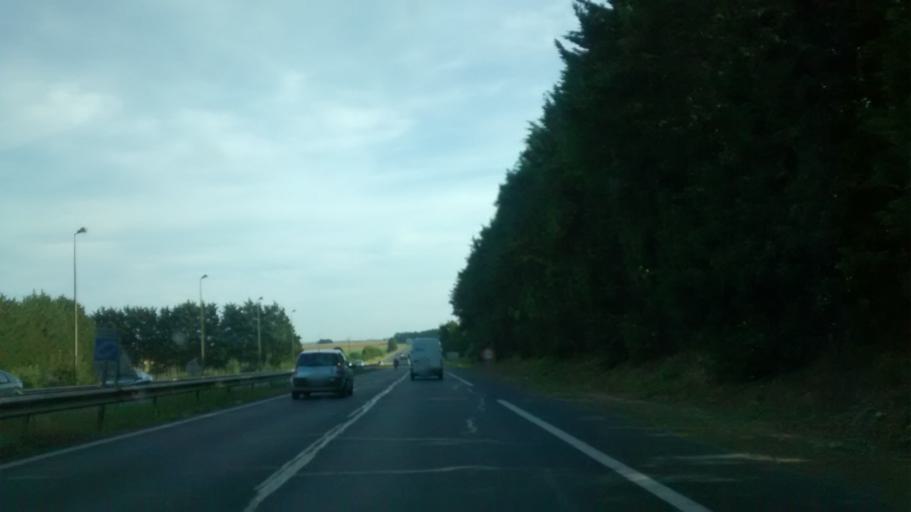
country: FR
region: Lower Normandy
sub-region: Departement du Calvados
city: Authie
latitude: 49.1868
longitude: -0.4247
